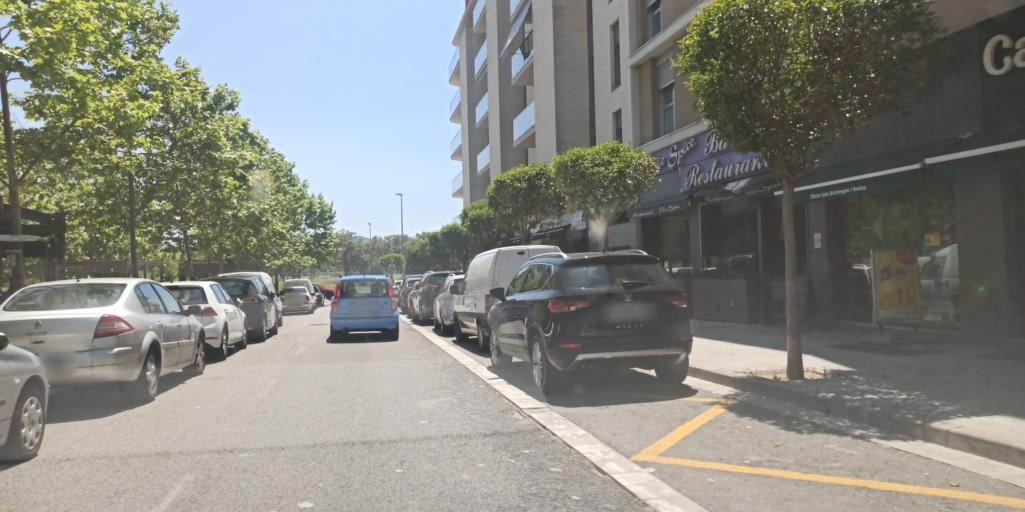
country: ES
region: Catalonia
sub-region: Provincia de Barcelona
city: Vilafranca del Penedes
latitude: 41.3359
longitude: 1.7018
